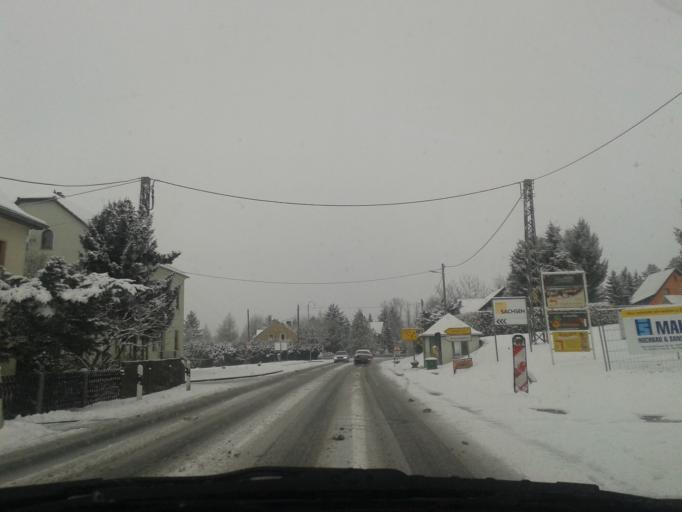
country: DE
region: Saxony
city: Rammenau
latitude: 51.1514
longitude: 14.1491
